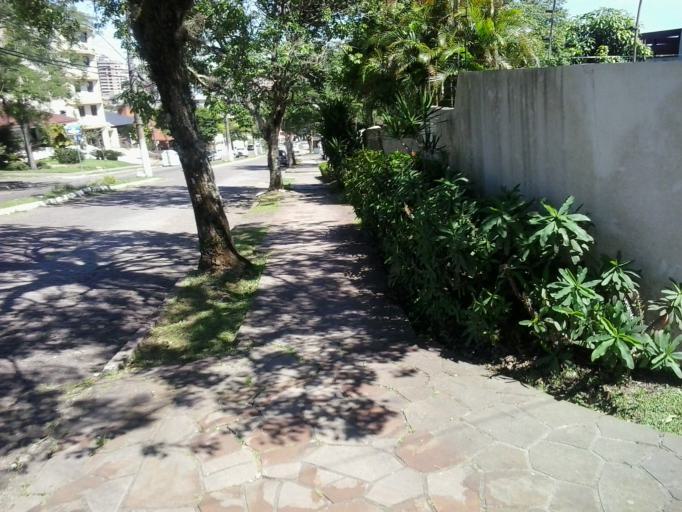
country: BR
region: Rio Grande do Sul
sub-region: Santa Maria
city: Santa Maria
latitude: -29.6989
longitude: -53.7938
